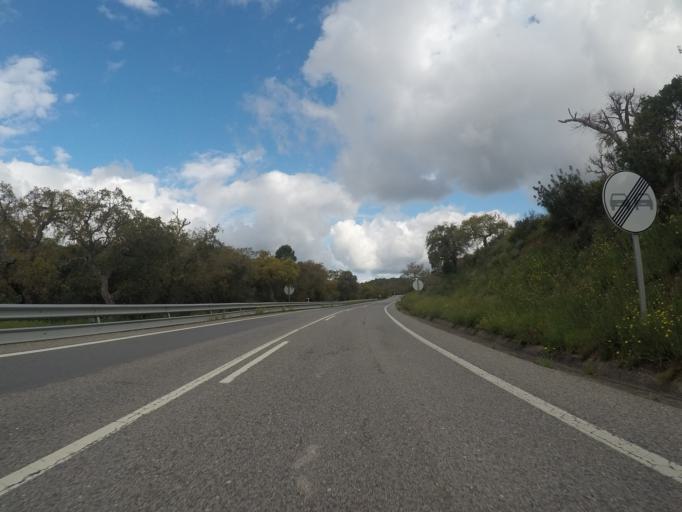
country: PT
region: Faro
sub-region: Lagos
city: Lagos
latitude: 37.1799
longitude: -8.7574
